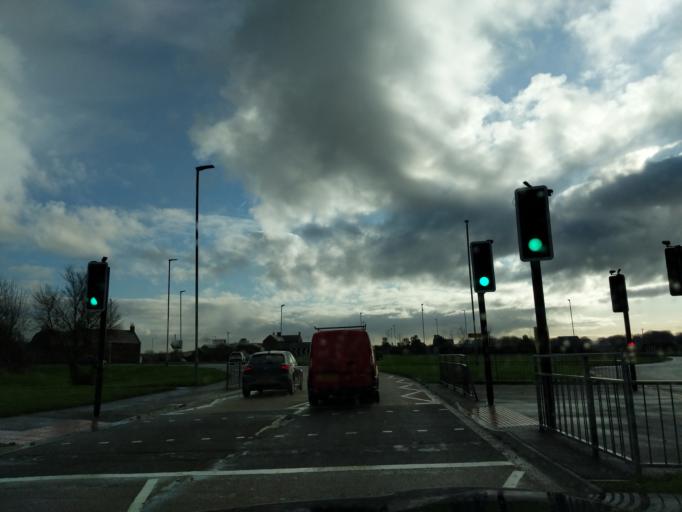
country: GB
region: England
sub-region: Northumberland
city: Blyth
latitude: 55.1099
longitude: -1.5034
